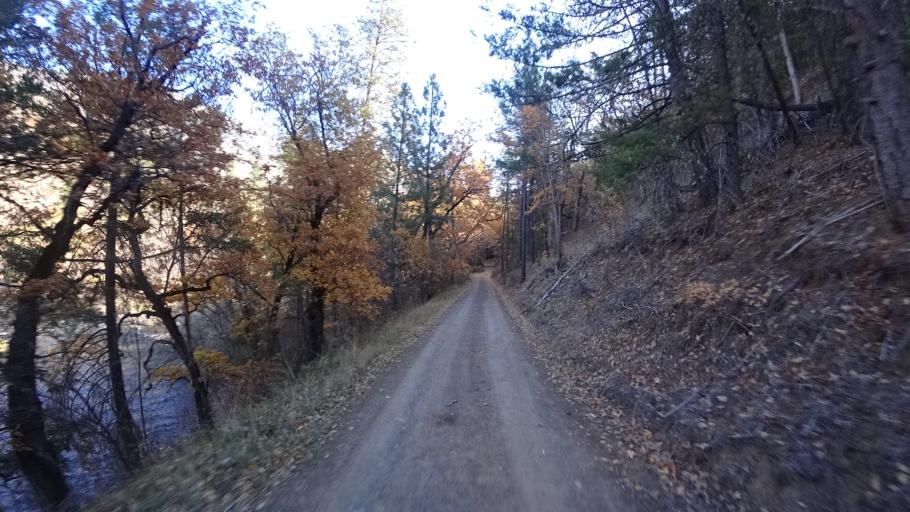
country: US
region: California
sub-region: Siskiyou County
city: Yreka
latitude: 41.8643
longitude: -122.7972
